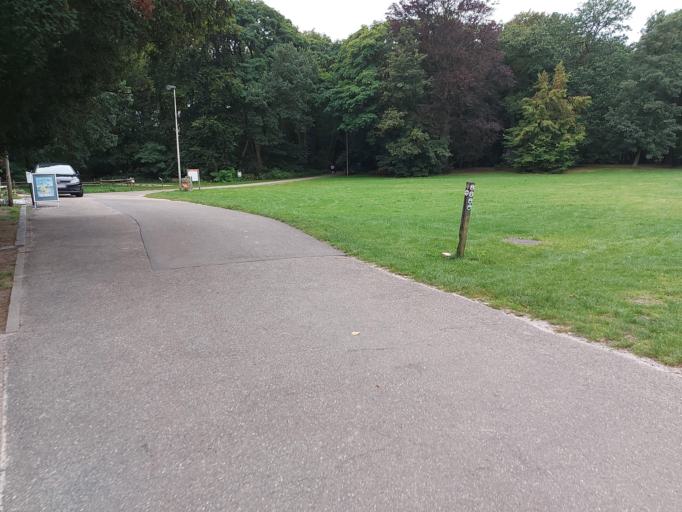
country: BE
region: Flanders
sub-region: Provincie Limburg
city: Zonhoven
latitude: 50.9609
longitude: 5.3765
